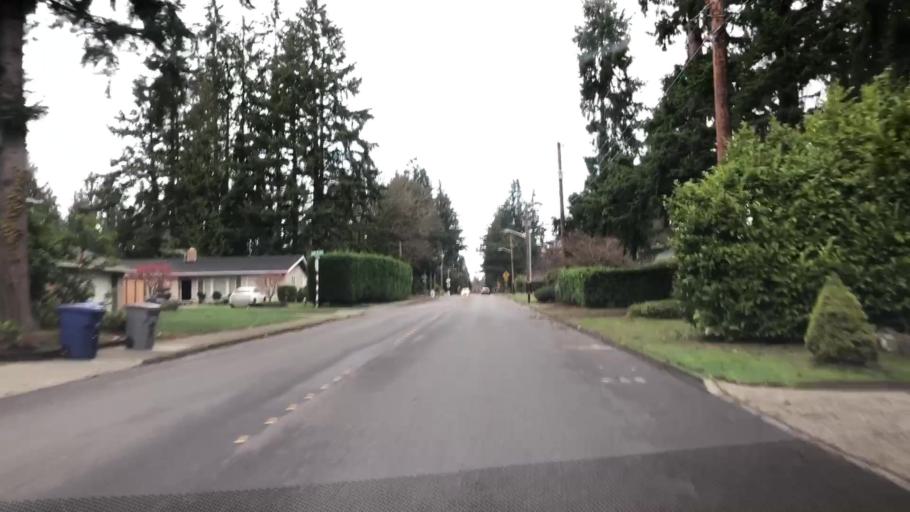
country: US
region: Washington
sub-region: King County
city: West Lake Sammamish
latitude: 47.6121
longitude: -122.1214
